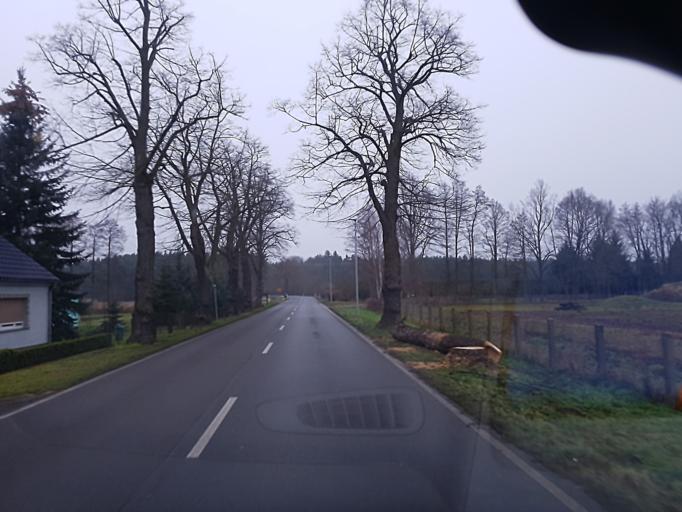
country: DE
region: Brandenburg
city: Luebben
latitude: 51.8896
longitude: 13.9008
